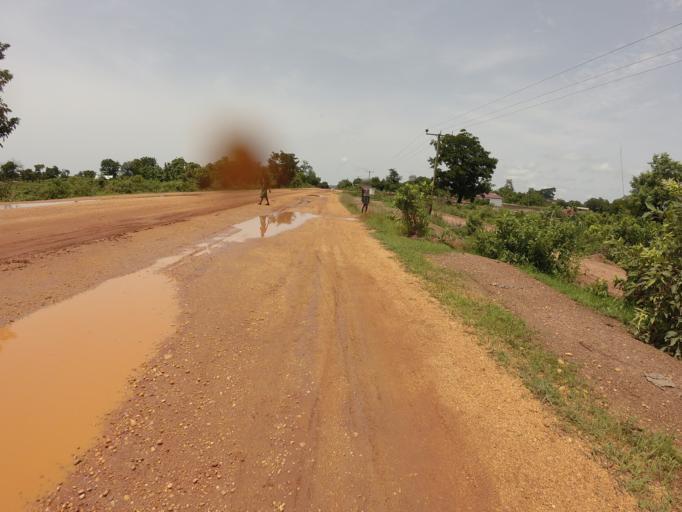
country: GH
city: Kpandae
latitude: 8.7093
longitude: 0.1528
